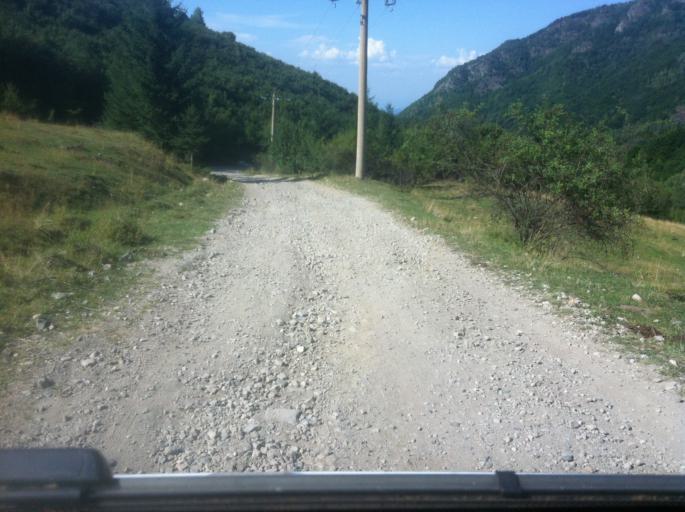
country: RO
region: Hunedoara
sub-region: Comuna Rau de Mori
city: Rau de Mori
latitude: 45.4484
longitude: 22.8953
